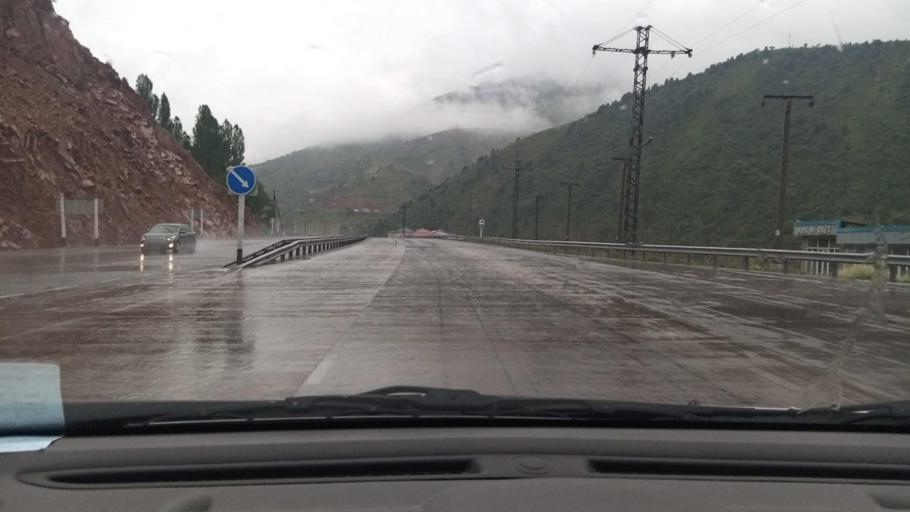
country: UZ
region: Toshkent
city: Angren
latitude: 41.1510
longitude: 70.4297
